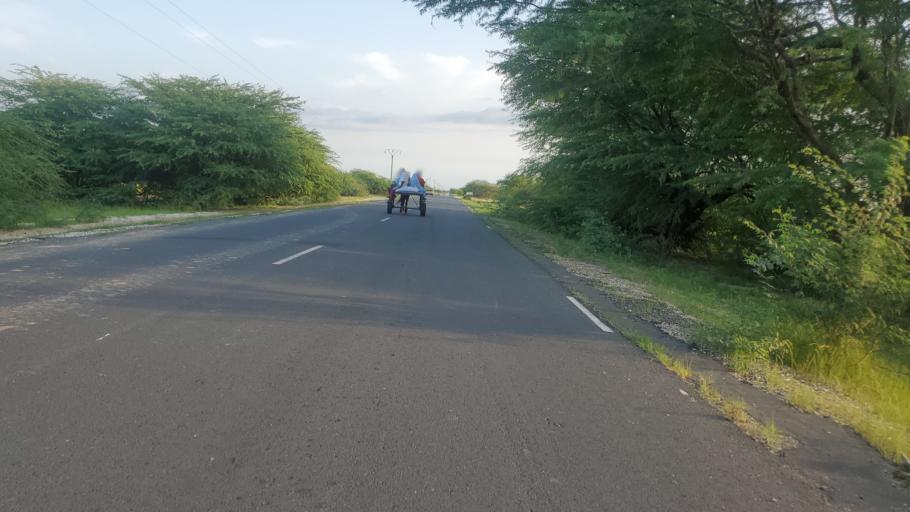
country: SN
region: Saint-Louis
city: Saint-Louis
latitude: 16.1882
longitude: -16.4093
